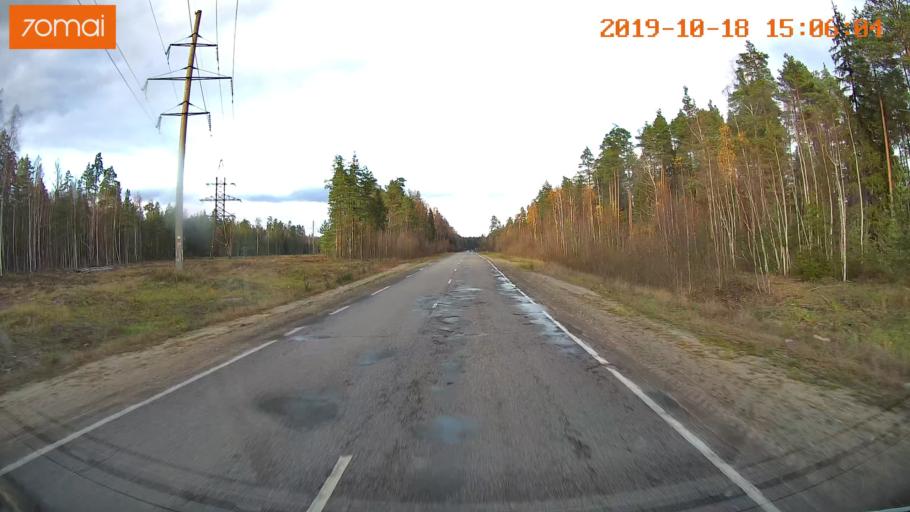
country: RU
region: Vladimir
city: Gus'-Khrustal'nyy
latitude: 55.5244
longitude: 40.5760
